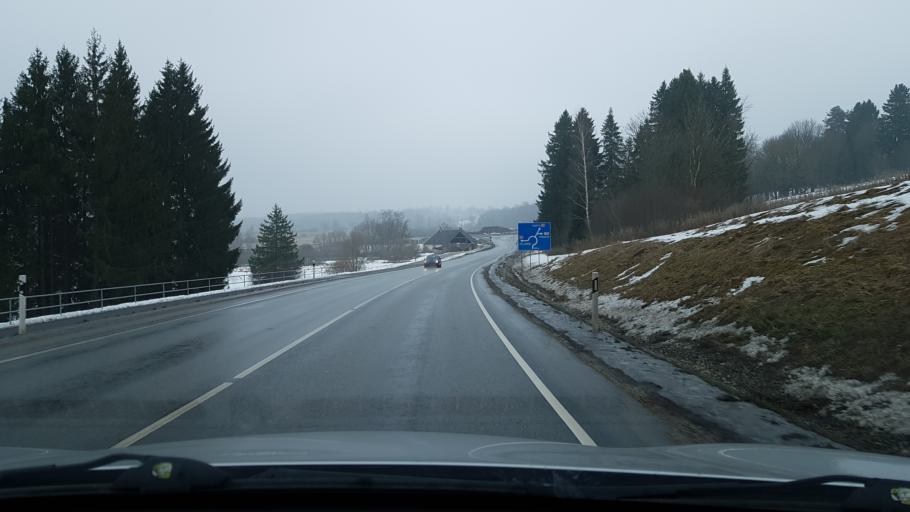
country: EE
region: Viljandimaa
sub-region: Viiratsi vald
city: Viiratsi
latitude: 58.3599
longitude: 25.6308
